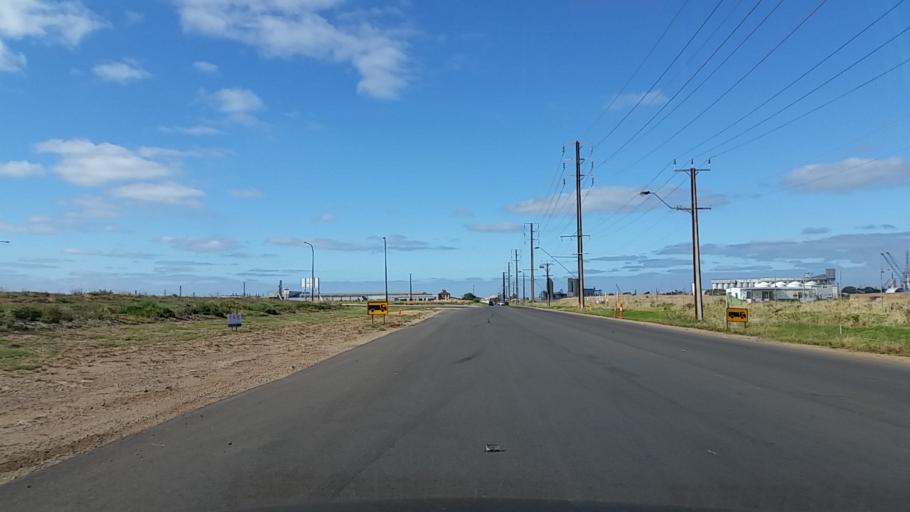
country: AU
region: South Australia
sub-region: Port Adelaide Enfield
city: Birkenhead
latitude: -34.8174
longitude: 138.5250
